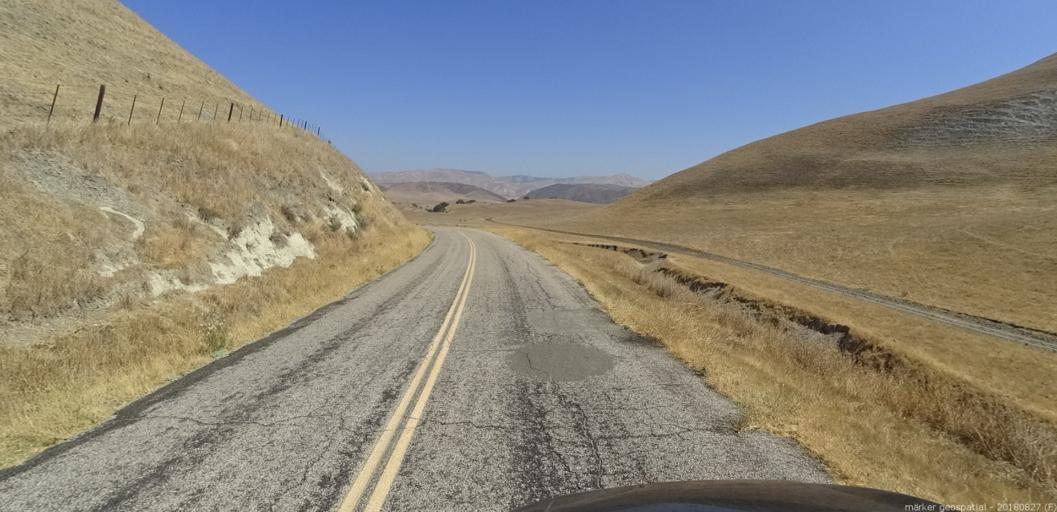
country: US
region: California
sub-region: Monterey County
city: King City
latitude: 36.2521
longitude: -120.9990
